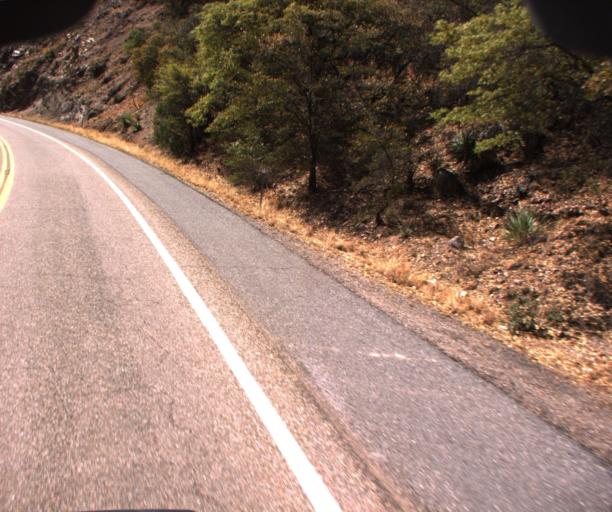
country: US
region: Arizona
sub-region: Cochise County
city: Bisbee
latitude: 31.4468
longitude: -109.9297
